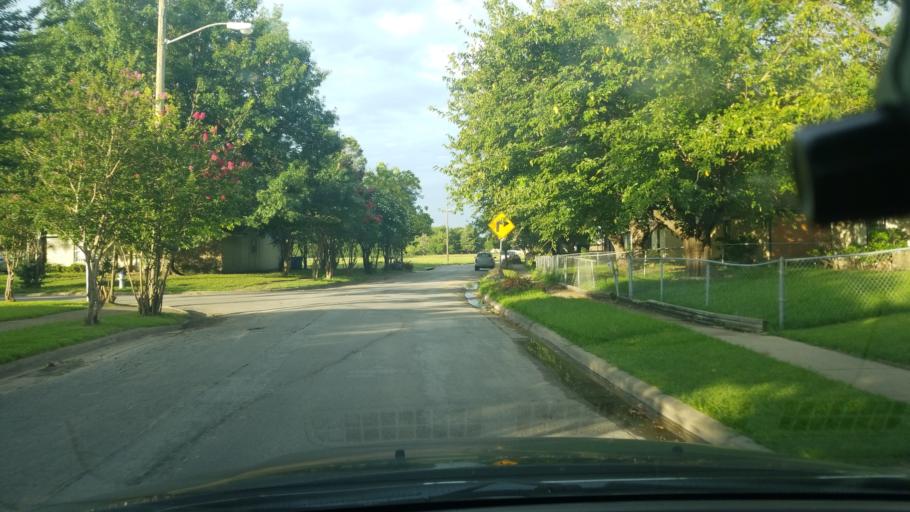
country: US
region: Texas
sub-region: Dallas County
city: Balch Springs
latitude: 32.7441
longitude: -96.6513
